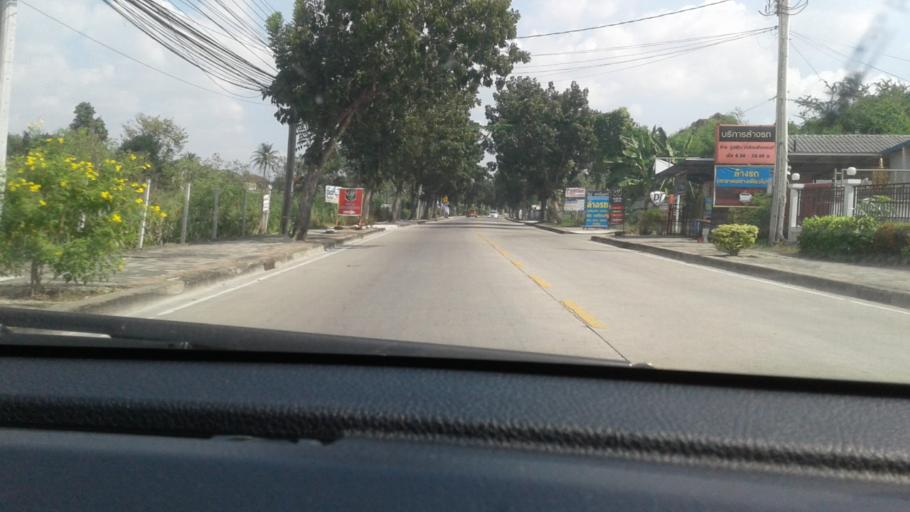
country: TH
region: Bangkok
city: Taling Chan
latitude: 13.7896
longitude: 100.4064
